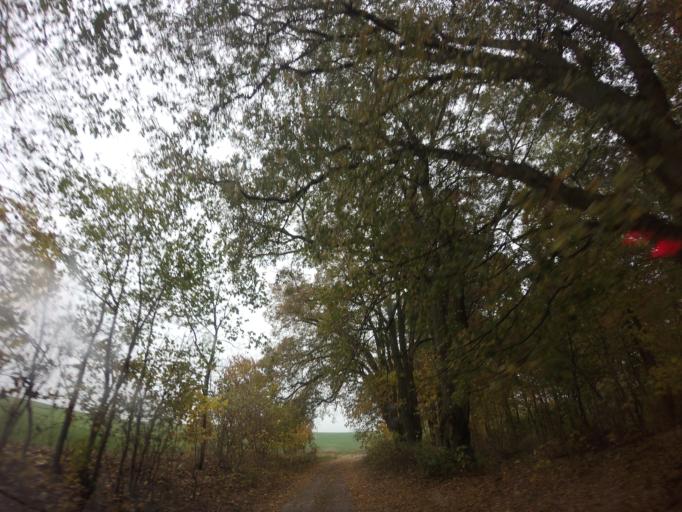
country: PL
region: West Pomeranian Voivodeship
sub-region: Powiat choszczenski
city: Krzecin
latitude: 53.0088
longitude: 15.4249
